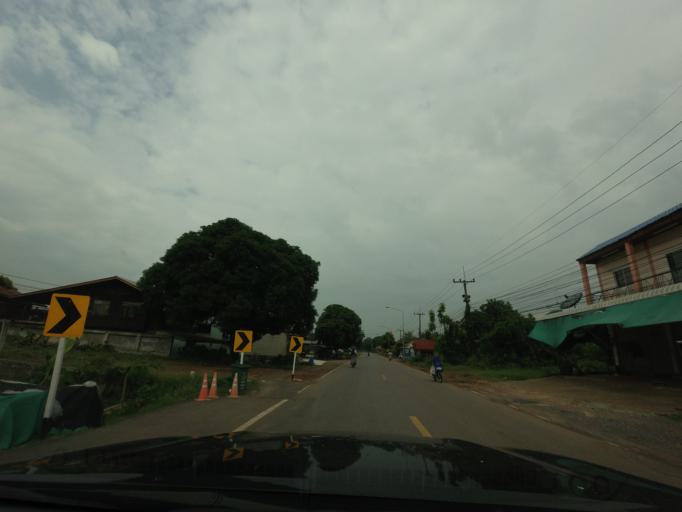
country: TH
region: Nong Khai
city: Tha Bo
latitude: 17.7997
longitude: 102.6669
